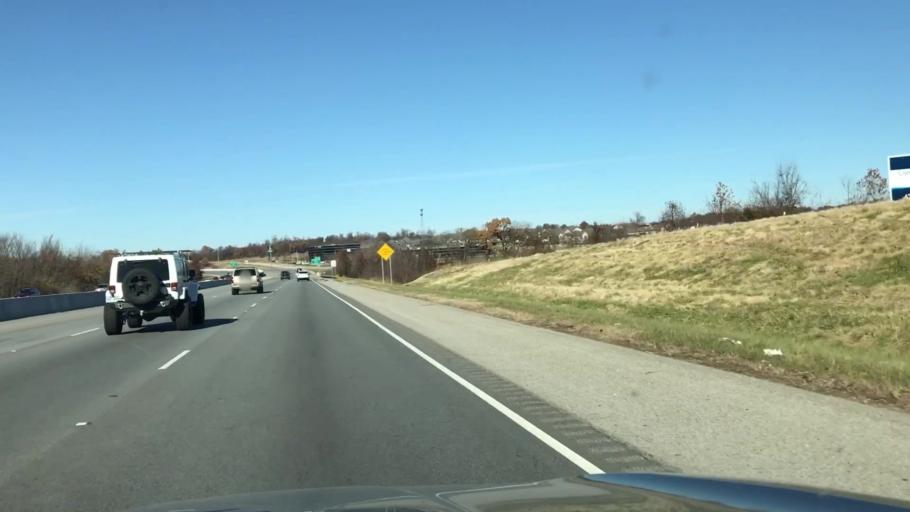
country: US
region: Arkansas
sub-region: Benton County
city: Lowell
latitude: 36.2900
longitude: -94.1616
